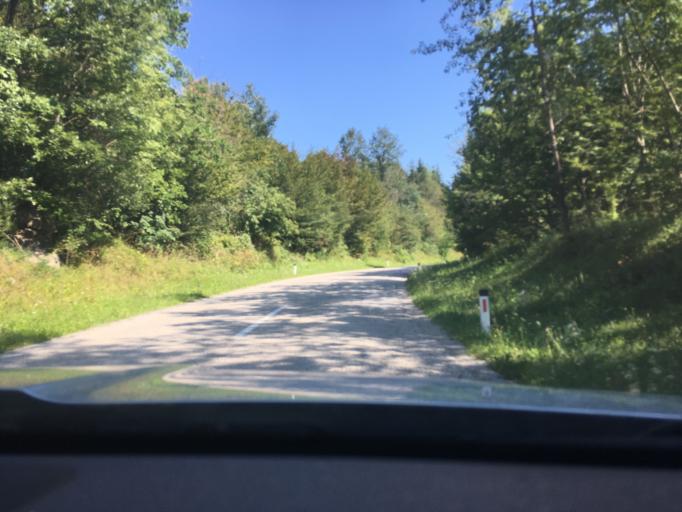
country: SI
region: Metlika
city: Metlika
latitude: 45.4990
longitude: 15.3483
